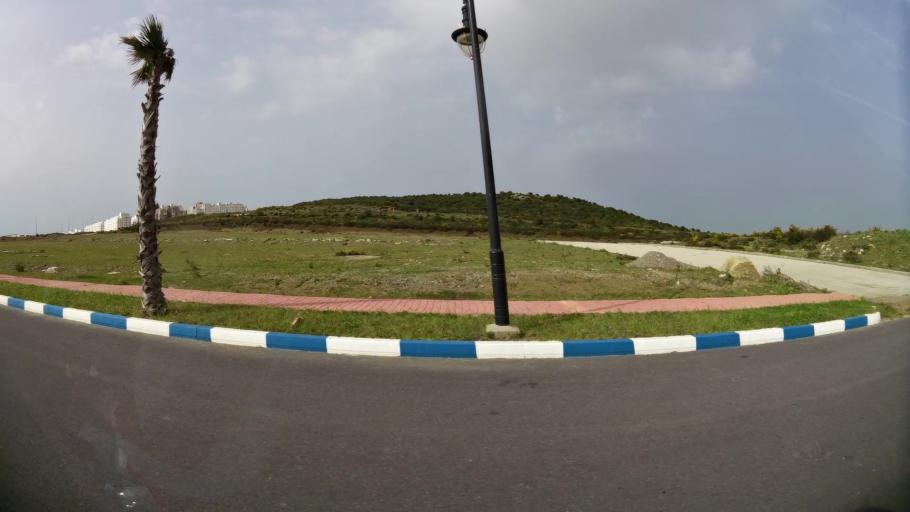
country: MA
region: Tanger-Tetouan
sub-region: Tanger-Assilah
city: Boukhalef
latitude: 35.6979
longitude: -5.9280
